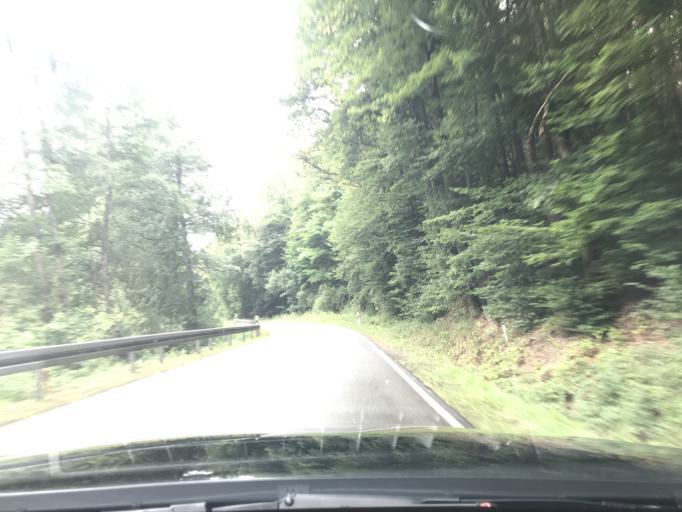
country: DE
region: Bavaria
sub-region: Regierungsbezirk Unterfranken
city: Breitbrunn
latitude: 50.0375
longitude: 10.6665
